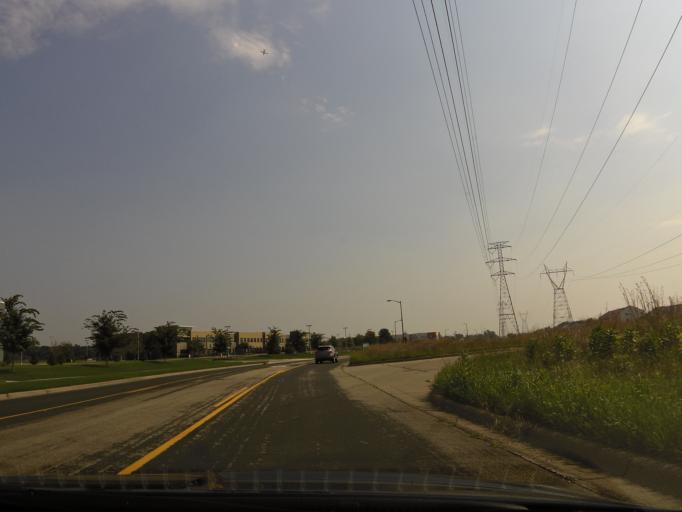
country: US
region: Minnesota
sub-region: Scott County
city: Shakopee
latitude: 44.7809
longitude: -93.4633
